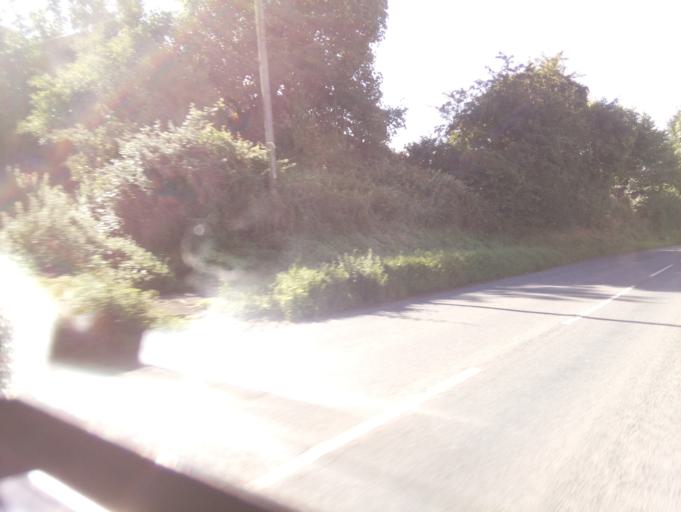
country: GB
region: England
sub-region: Herefordshire
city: Walford
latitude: 51.8950
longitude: -2.5899
